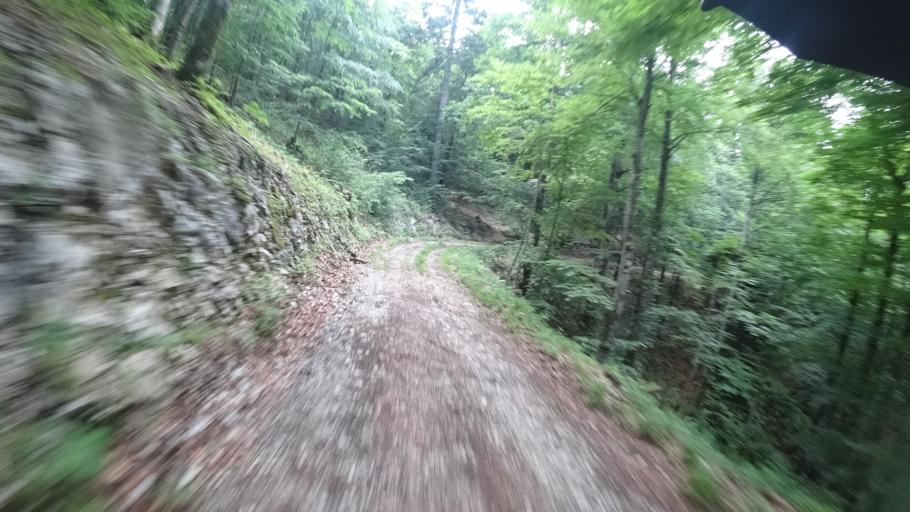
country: SI
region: Osilnica
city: Osilnica
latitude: 45.4885
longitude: 14.6820
